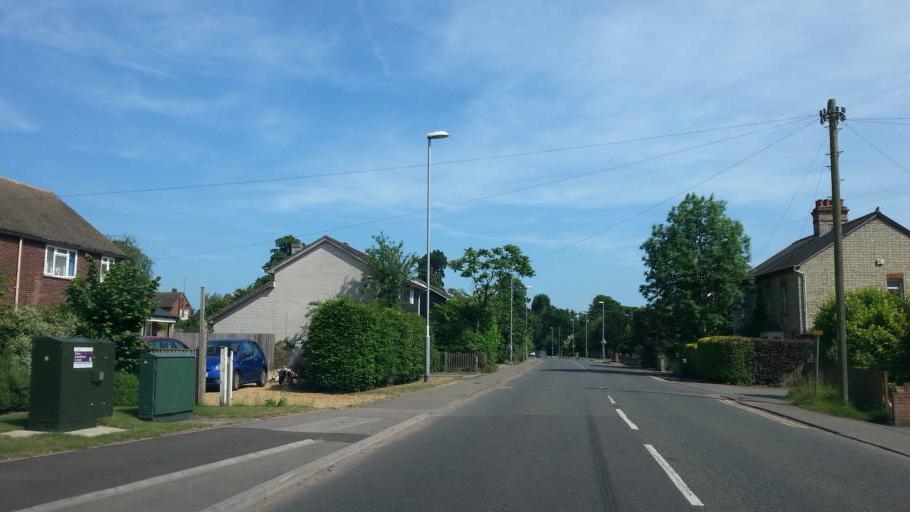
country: GB
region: England
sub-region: Cambridgeshire
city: Sawston
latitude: 52.1456
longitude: 0.1423
